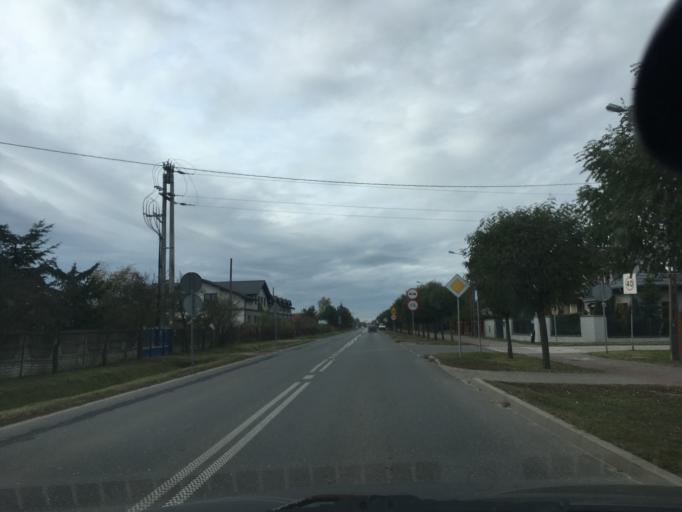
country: PL
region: Masovian Voivodeship
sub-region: Powiat zyrardowski
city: Mszczonow
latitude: 51.9736
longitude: 20.5368
